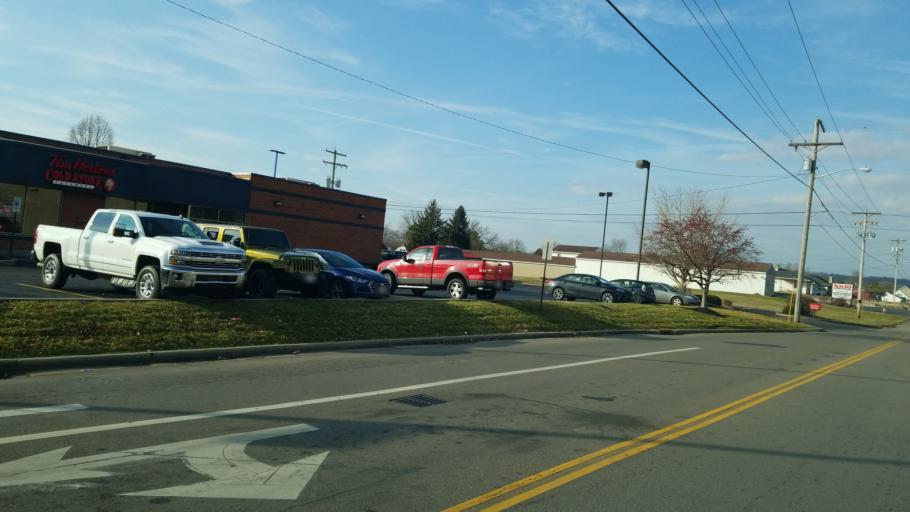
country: US
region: Ohio
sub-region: Ross County
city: Chillicothe
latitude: 39.3563
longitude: -82.9761
